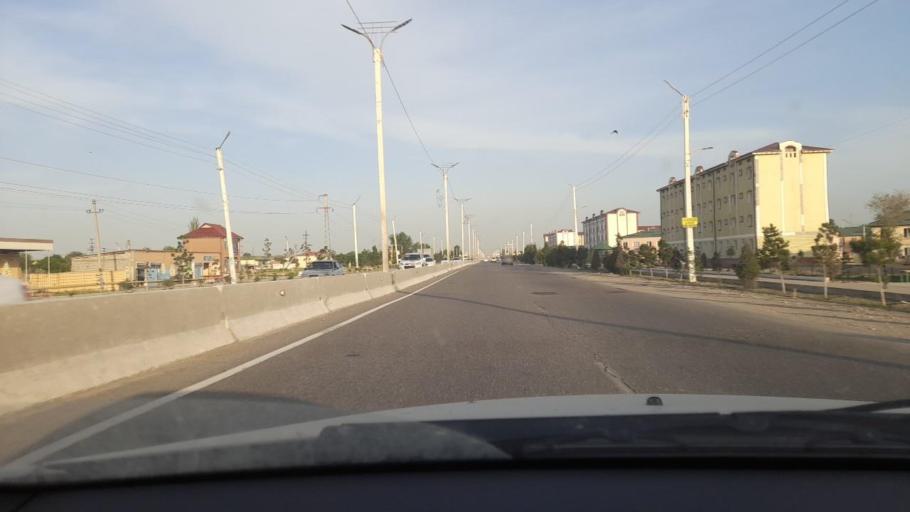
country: KZ
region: Ongtustik Qazaqstan
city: Myrzakent
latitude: 40.5449
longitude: 68.4123
